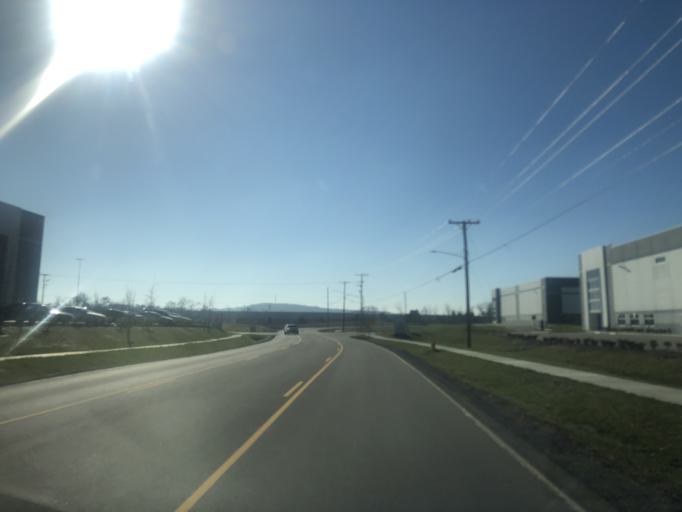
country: US
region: Tennessee
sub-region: Rutherford County
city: La Vergne
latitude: 36.0055
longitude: -86.5836
